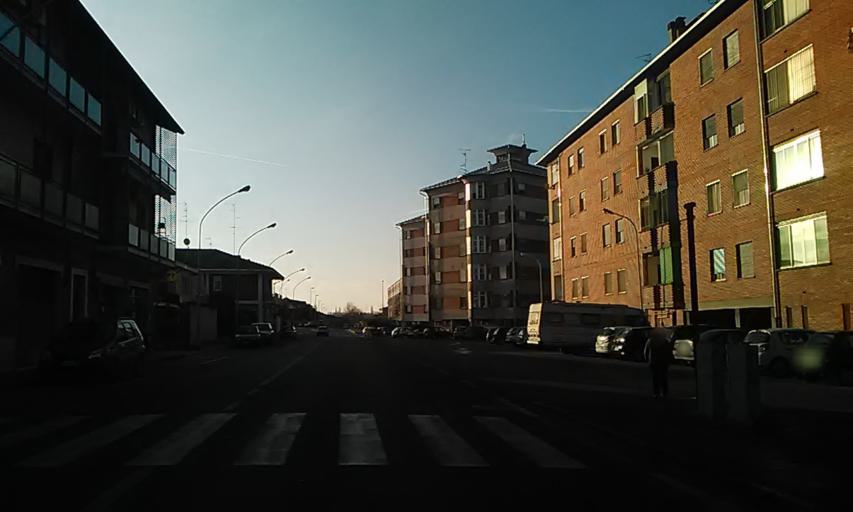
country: IT
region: Piedmont
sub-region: Provincia di Vercelli
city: Vercelli
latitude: 45.3192
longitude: 8.4070
